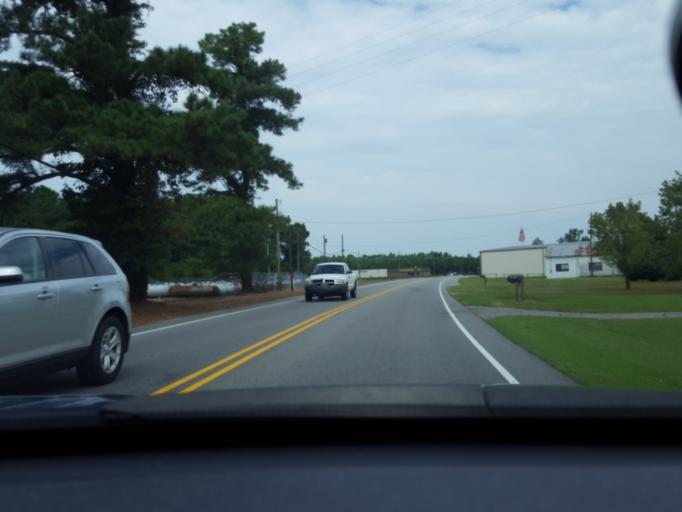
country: US
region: North Carolina
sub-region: Chowan County
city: Edenton
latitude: 36.1344
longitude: -76.6568
